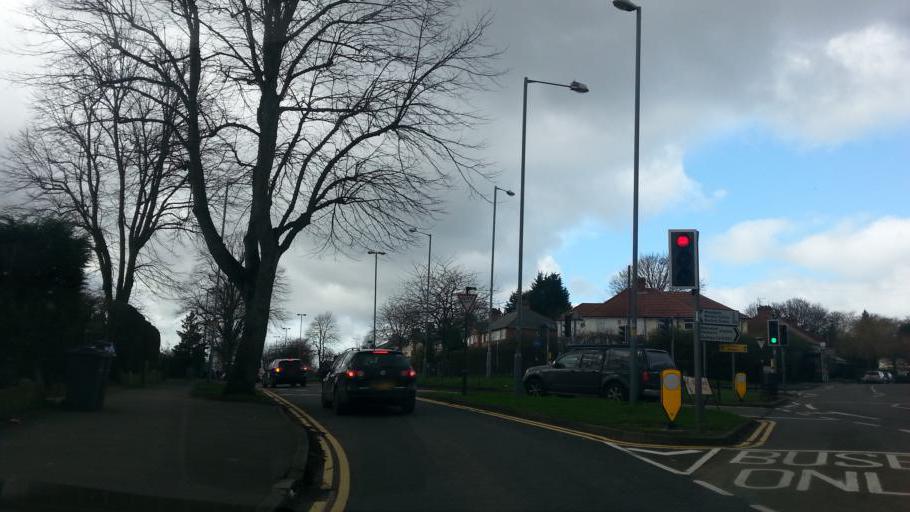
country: GB
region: England
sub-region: City and Borough of Birmingham
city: Bartley Green
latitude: 52.4484
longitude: -1.9473
